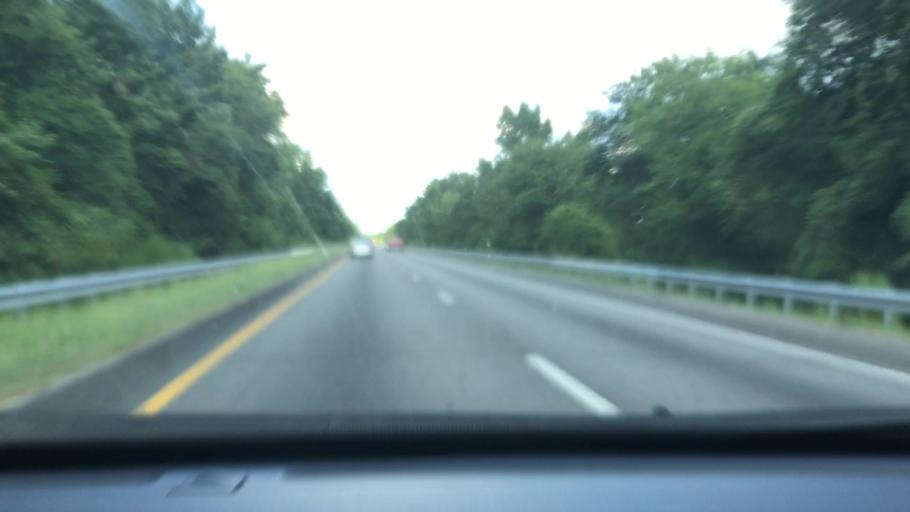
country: US
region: South Carolina
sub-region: Florence County
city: Florence
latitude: 34.2853
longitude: -79.6704
